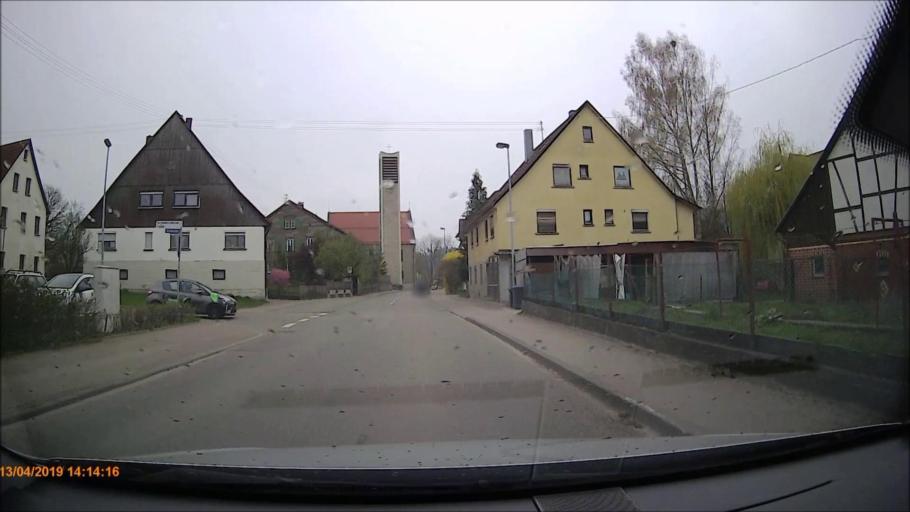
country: DE
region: Baden-Wuerttemberg
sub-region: Regierungsbezirk Stuttgart
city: Oberrot
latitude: 49.0076
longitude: 9.6782
